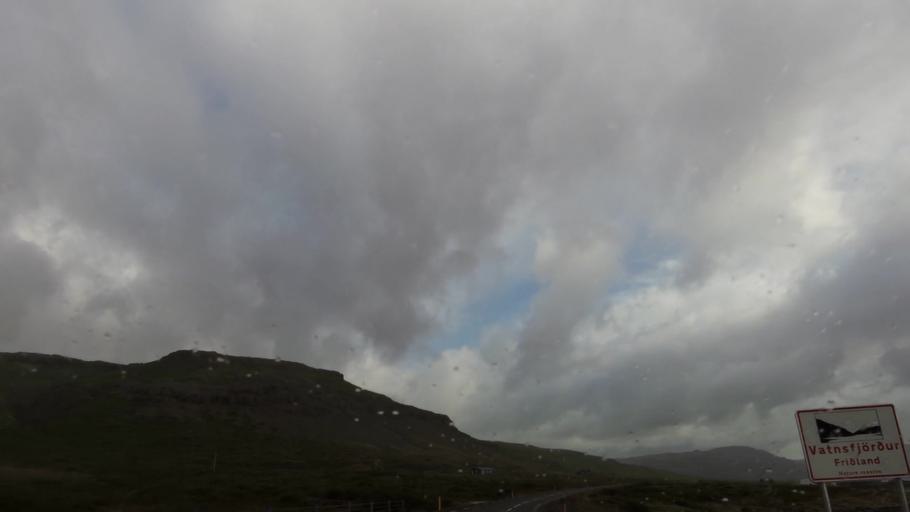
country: IS
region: Westfjords
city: Isafjoerdur
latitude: 65.5472
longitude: -23.2025
